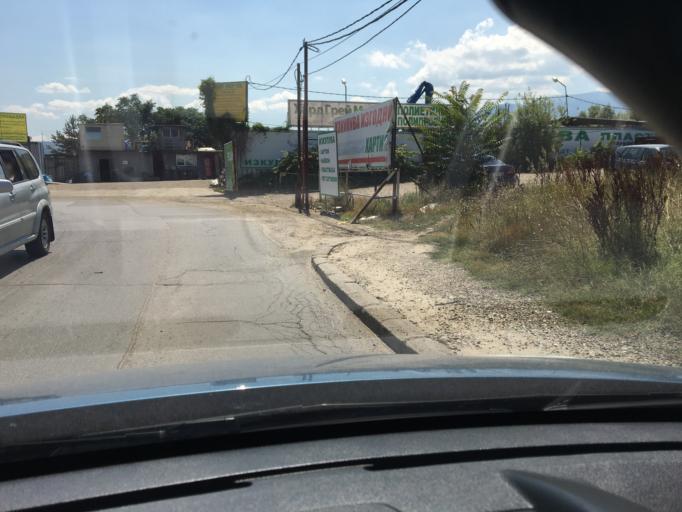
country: BG
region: Sofia-Capital
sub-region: Stolichna Obshtina
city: Sofia
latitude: 42.6373
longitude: 23.3976
